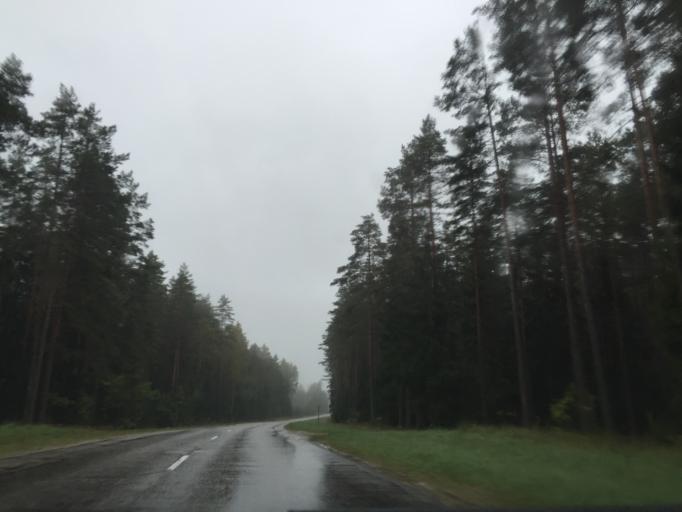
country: LV
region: Ropazu
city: Ropazi
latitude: 57.0215
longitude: 24.6835
